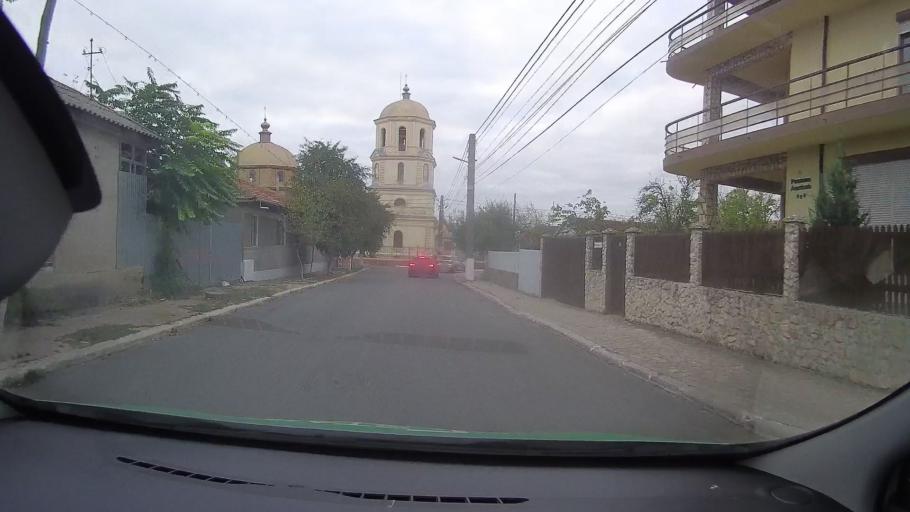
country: RO
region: Tulcea
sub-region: Comuna Jurilovca
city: Jurilovca
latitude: 44.7570
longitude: 28.8759
